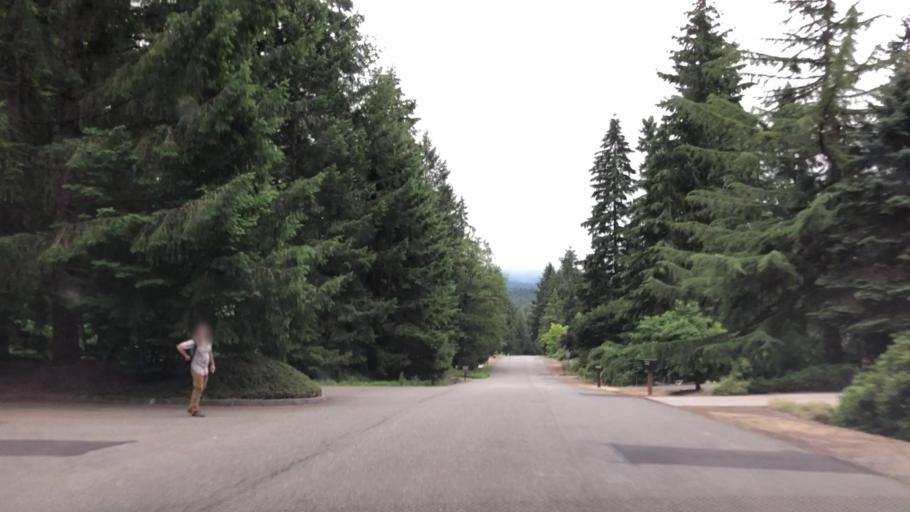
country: US
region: Washington
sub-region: King County
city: Cottage Lake
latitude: 47.7215
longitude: -122.0940
